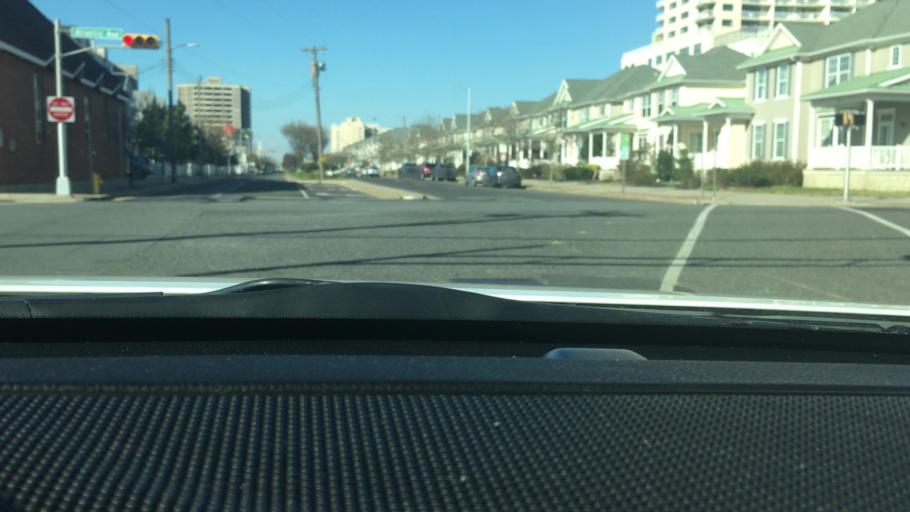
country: US
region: New Jersey
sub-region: Atlantic County
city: Atlantic City
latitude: 39.3681
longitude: -74.4129
